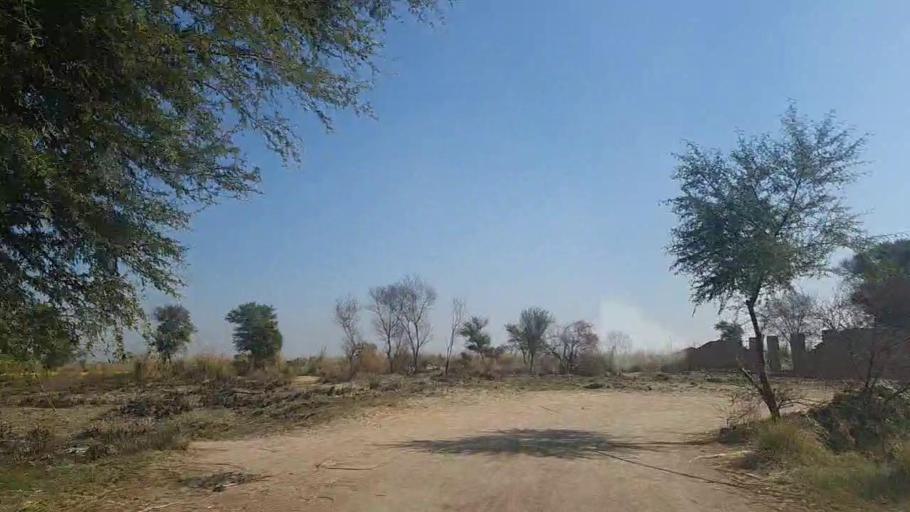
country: PK
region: Sindh
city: Sinjhoro
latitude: 26.1588
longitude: 68.8600
